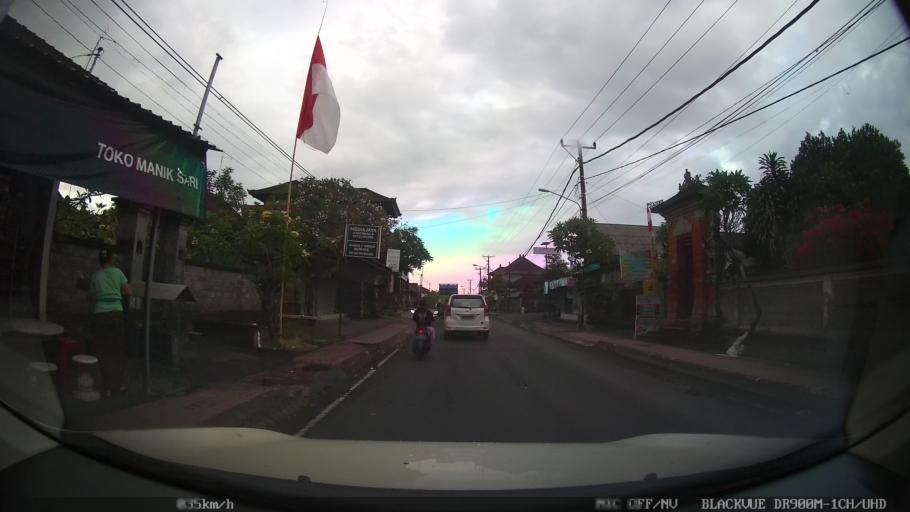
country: ID
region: Bali
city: Banjar Pasekan
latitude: -8.6200
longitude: 115.2841
